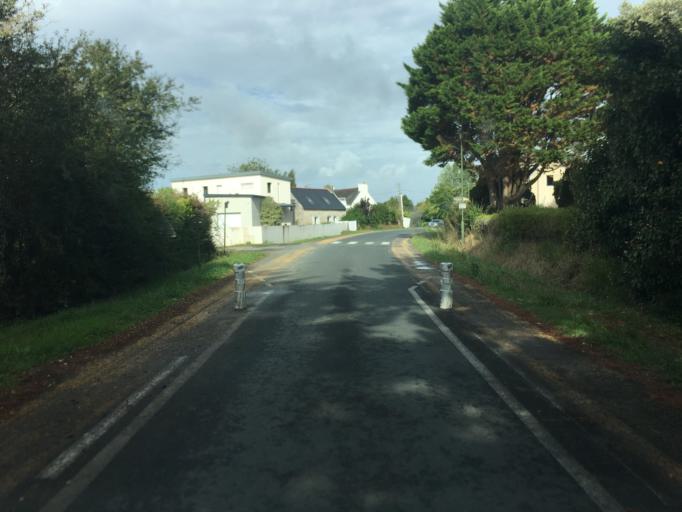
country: FR
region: Brittany
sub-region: Departement du Finistere
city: Plobannalec-Lesconil
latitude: 47.8154
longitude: -4.1925
